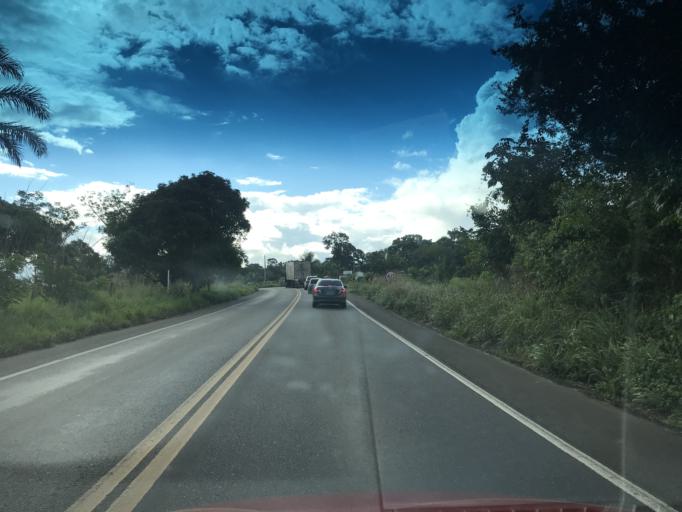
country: BR
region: Bahia
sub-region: Ibirapitanga
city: Ibirapitanga
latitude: -14.1532
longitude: -39.3282
